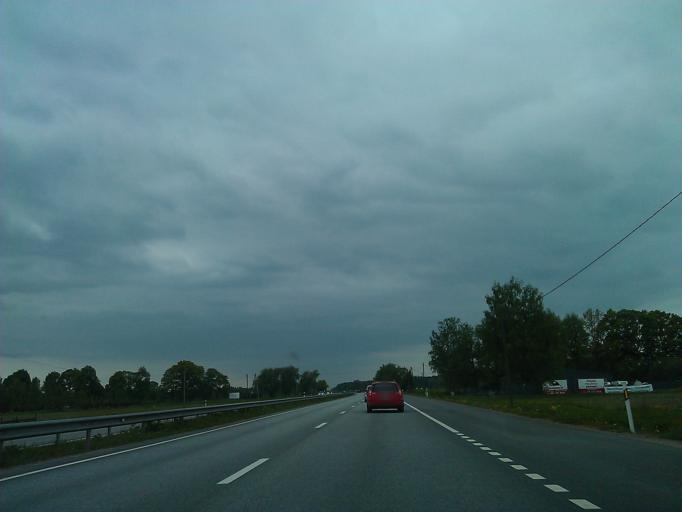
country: LV
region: Olaine
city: Olaine
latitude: 56.7761
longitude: 23.9346
